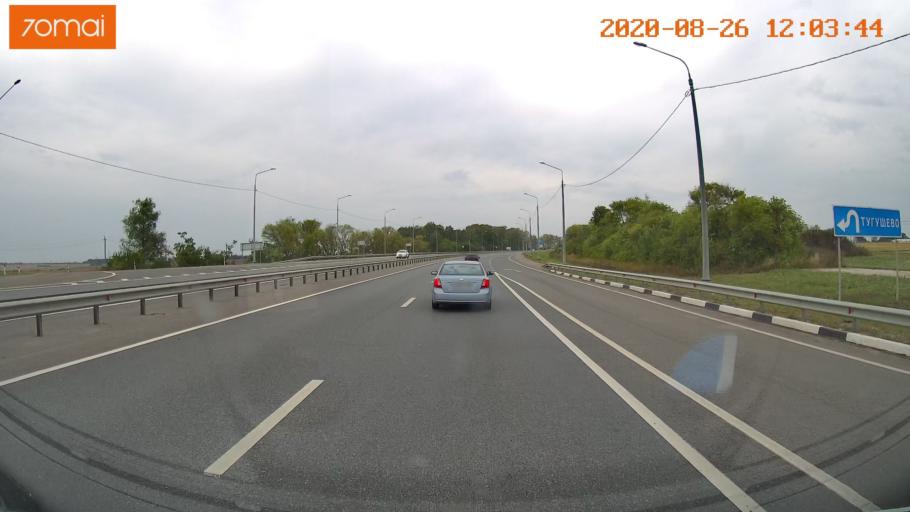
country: RU
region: Rjazan
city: Kiritsy
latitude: 54.3028
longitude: 40.2005
